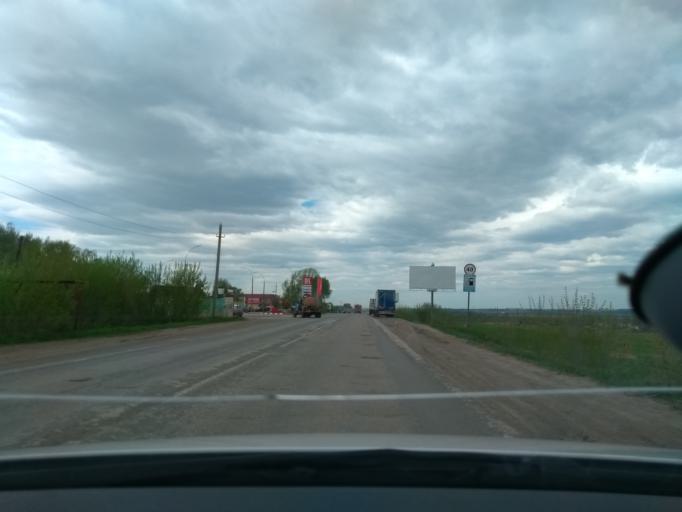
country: RU
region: Perm
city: Lobanovo
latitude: 57.8649
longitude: 56.2931
